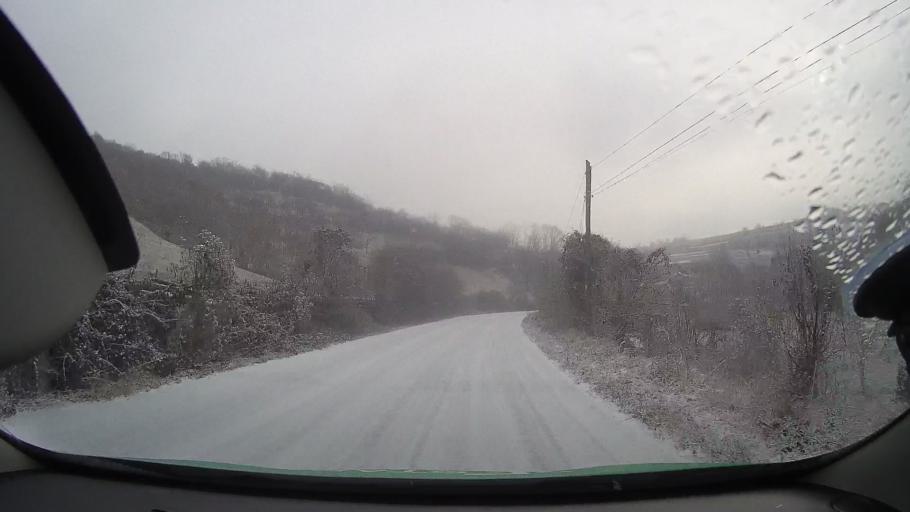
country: RO
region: Alba
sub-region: Comuna Livezile
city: Livezile
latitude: 46.3683
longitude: 23.5914
